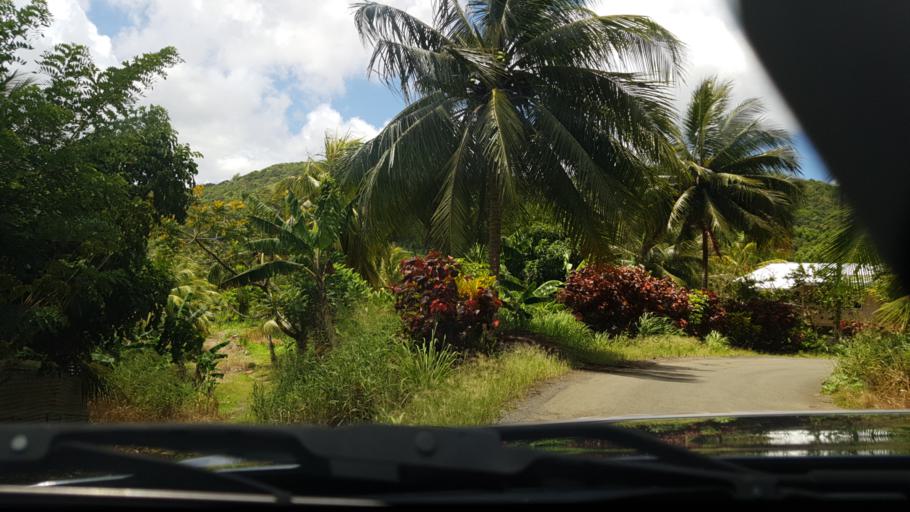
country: LC
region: Anse-la-Raye
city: Anse La Raye
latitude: 13.9518
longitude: -61.0003
